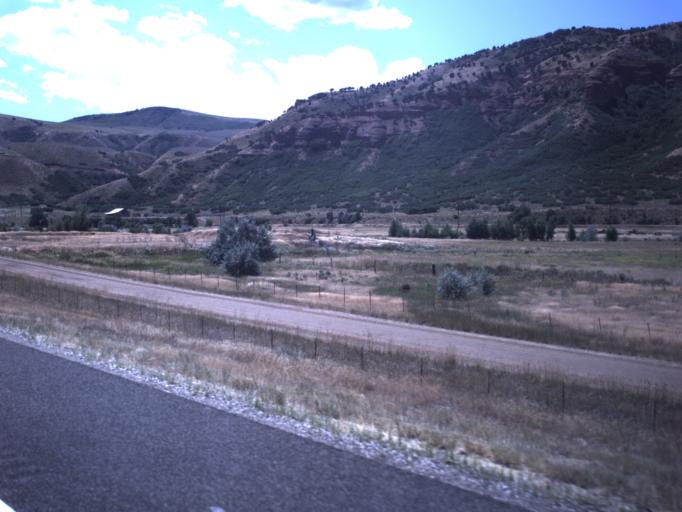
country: US
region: Utah
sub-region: Summit County
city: Coalville
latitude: 40.9807
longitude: -111.4477
